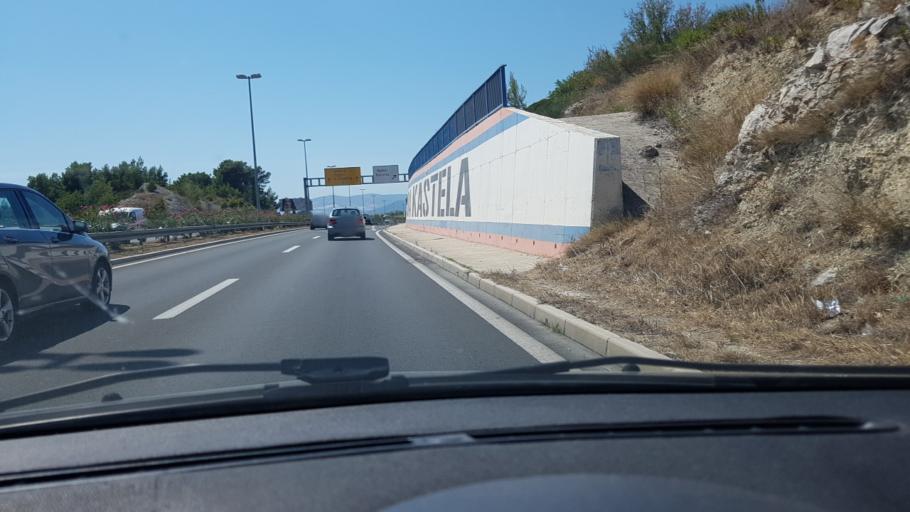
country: HR
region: Splitsko-Dalmatinska
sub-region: Grad Split
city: Split
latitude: 43.5512
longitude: 16.4198
